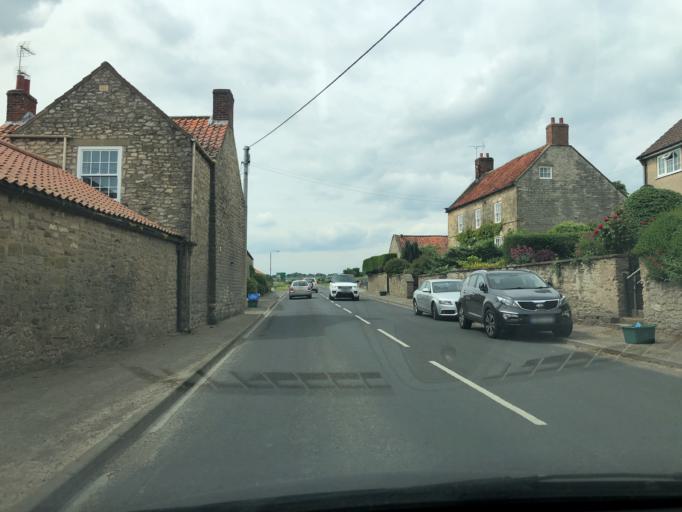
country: GB
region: England
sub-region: North Yorkshire
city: Pickering
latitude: 54.2615
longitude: -0.8123
